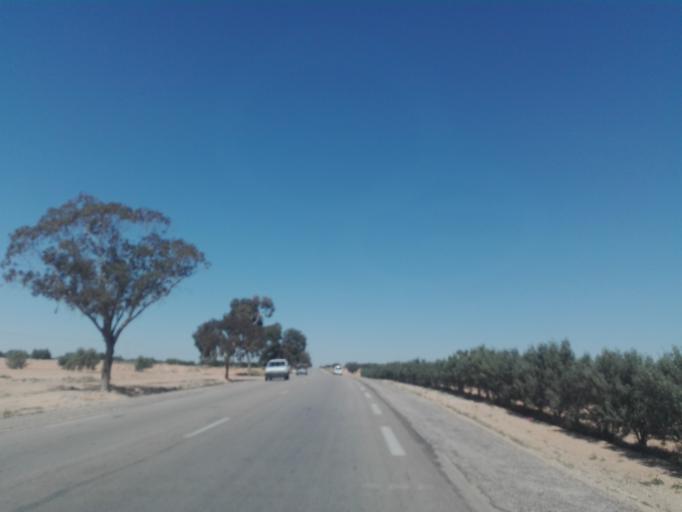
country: TN
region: Safaqis
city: Bi'r `Ali Bin Khalifah
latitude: 34.7503
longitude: 10.3477
